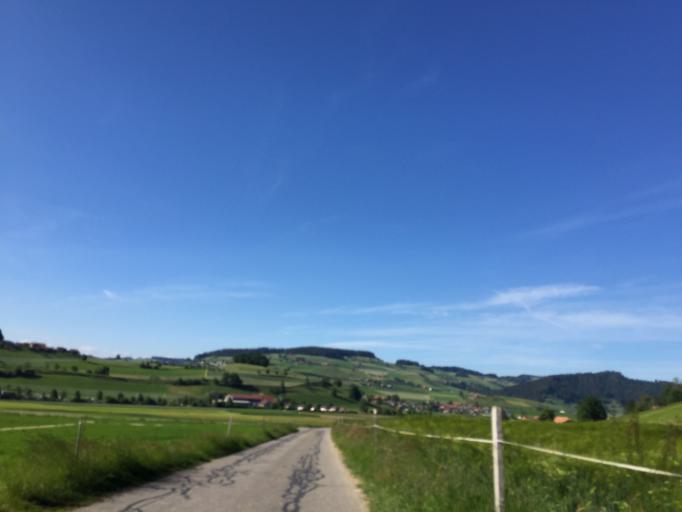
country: CH
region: Bern
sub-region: Bern-Mittelland District
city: Konolfingen
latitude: 46.8810
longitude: 7.6372
